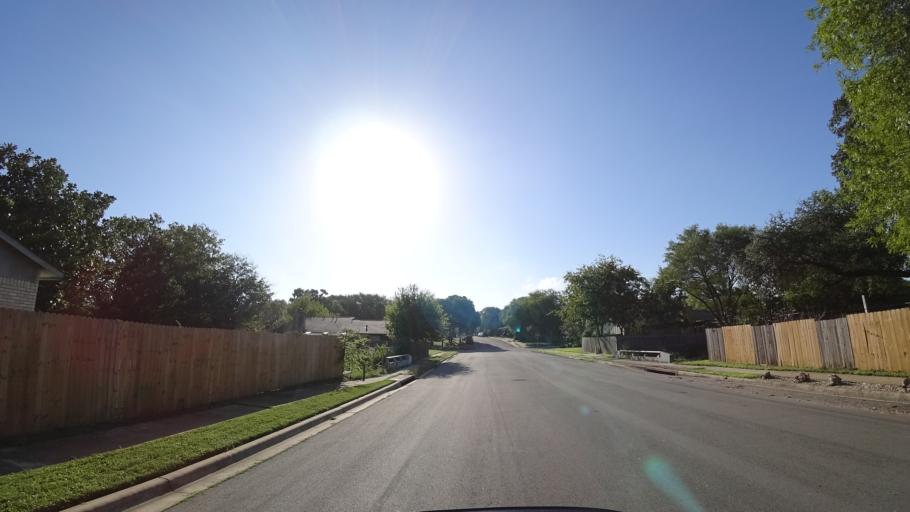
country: US
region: Texas
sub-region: Travis County
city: Rollingwood
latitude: 30.2148
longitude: -97.8133
